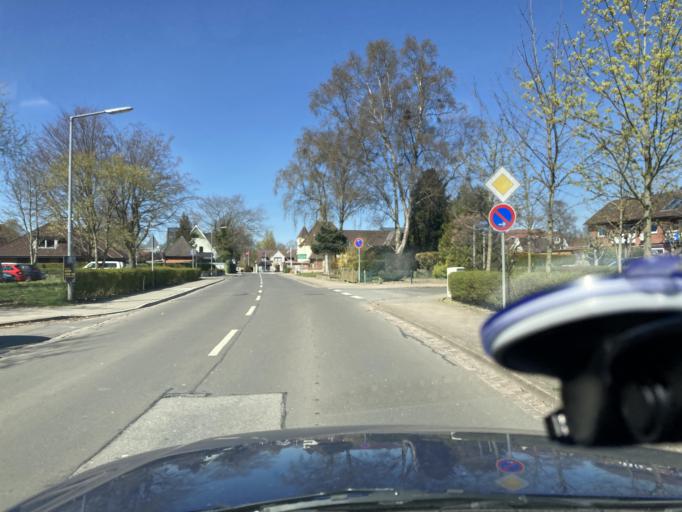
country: DE
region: Schleswig-Holstein
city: Heide
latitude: 54.1954
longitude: 9.1119
